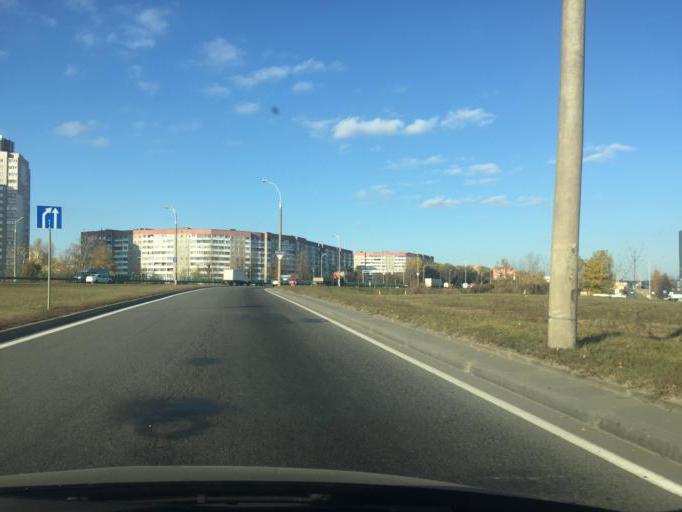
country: BY
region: Minsk
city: Vyaliki Trastsyanets
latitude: 53.8606
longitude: 27.6844
